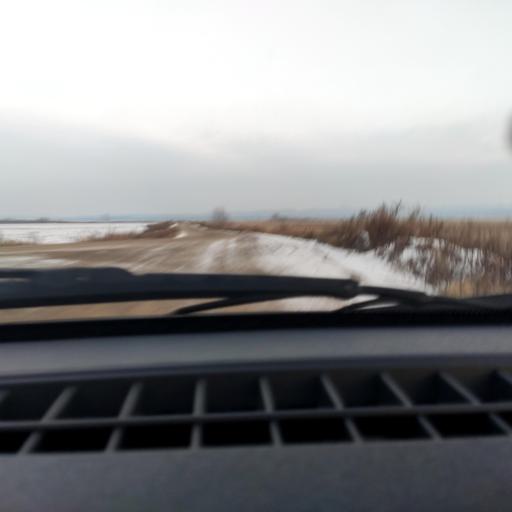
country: RU
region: Bashkortostan
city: Mikhaylovka
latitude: 54.8097
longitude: 55.9491
